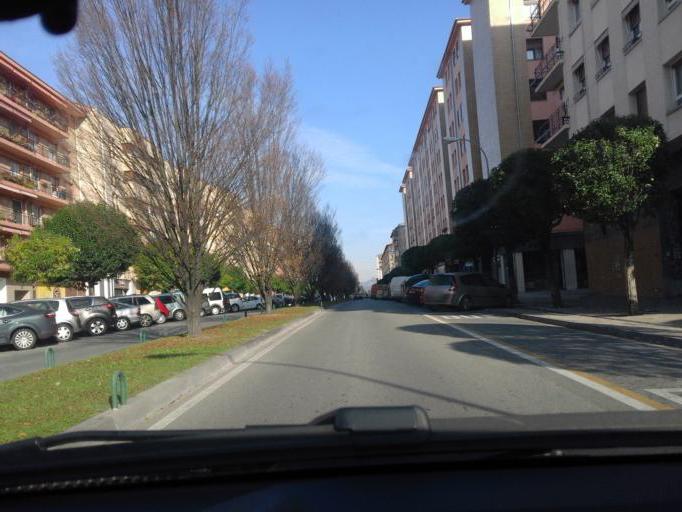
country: ES
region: Navarre
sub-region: Provincia de Navarra
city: Ermitagana
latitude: 42.8156
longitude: -1.6640
